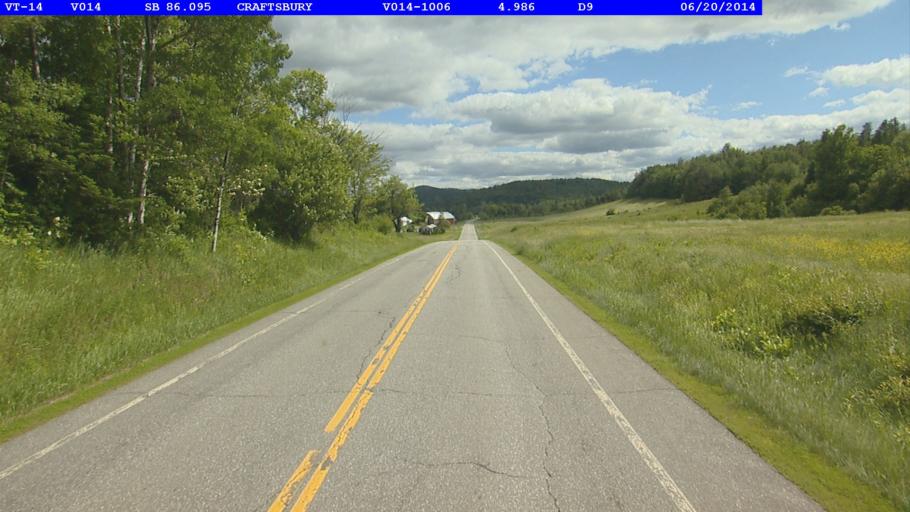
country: US
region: Vermont
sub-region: Caledonia County
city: Hardwick
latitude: 44.6624
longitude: -72.4034
